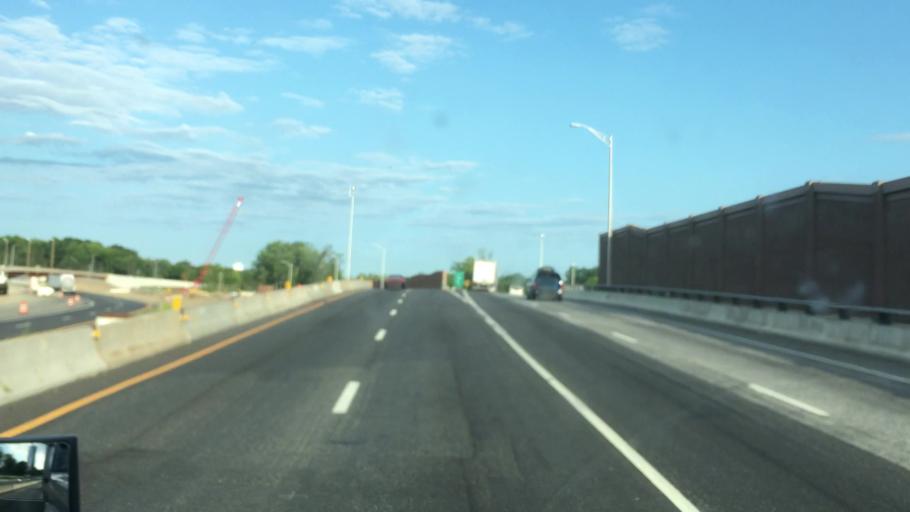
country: US
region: New Jersey
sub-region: Camden County
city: Mount Ephraim
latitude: 39.8745
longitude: -75.0961
